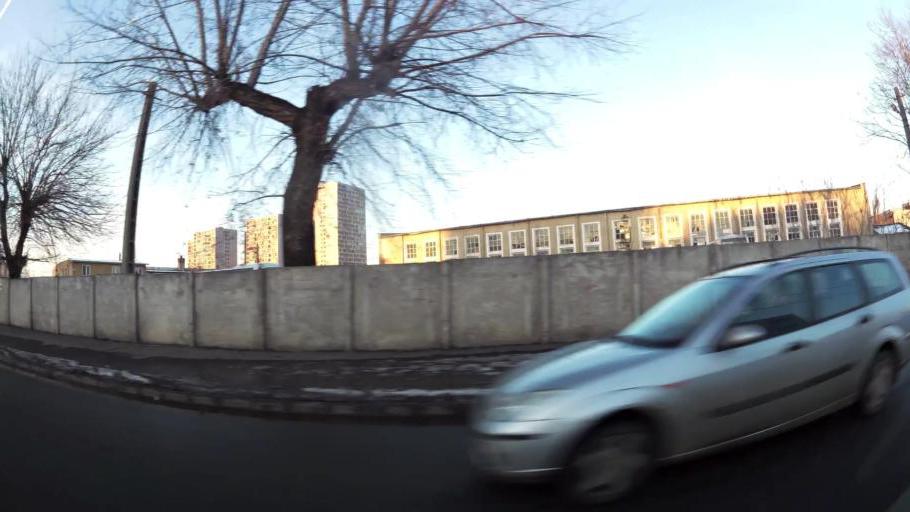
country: RO
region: Ilfov
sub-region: Comuna Fundeni-Dobroesti
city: Fundeni
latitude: 44.4486
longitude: 26.1449
